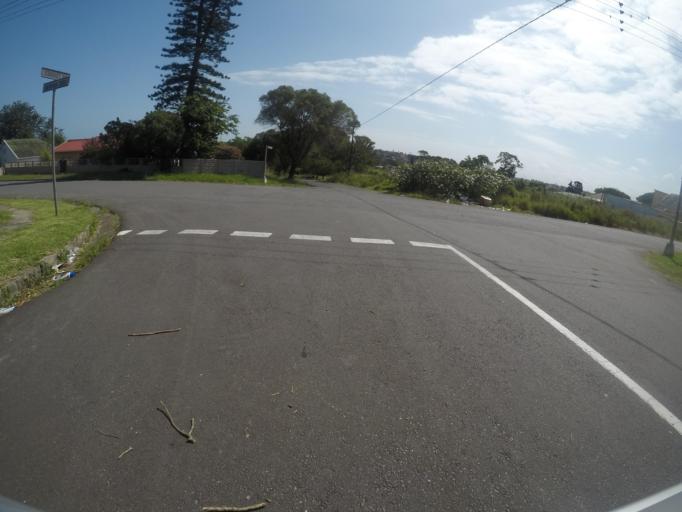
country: ZA
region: Eastern Cape
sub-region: Buffalo City Metropolitan Municipality
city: East London
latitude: -32.9809
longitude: 27.8738
